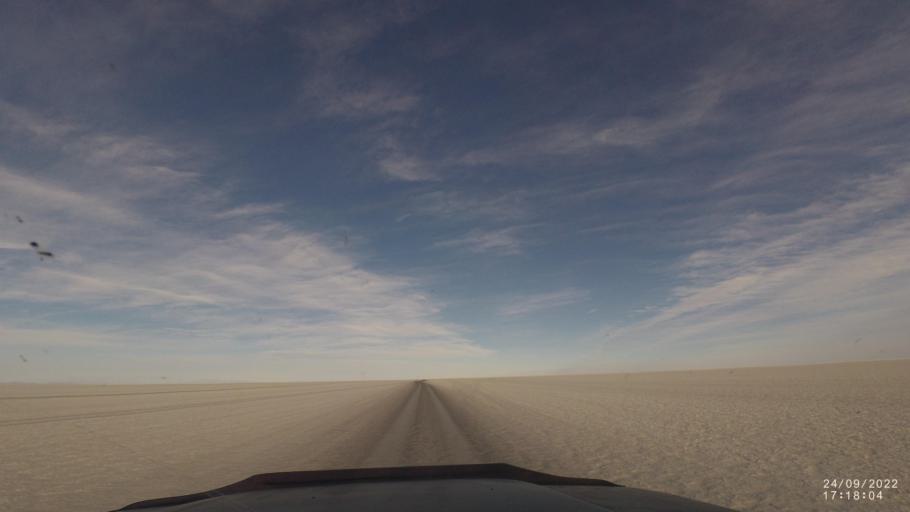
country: BO
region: Potosi
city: Colchani
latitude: -20.2407
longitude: -67.6167
